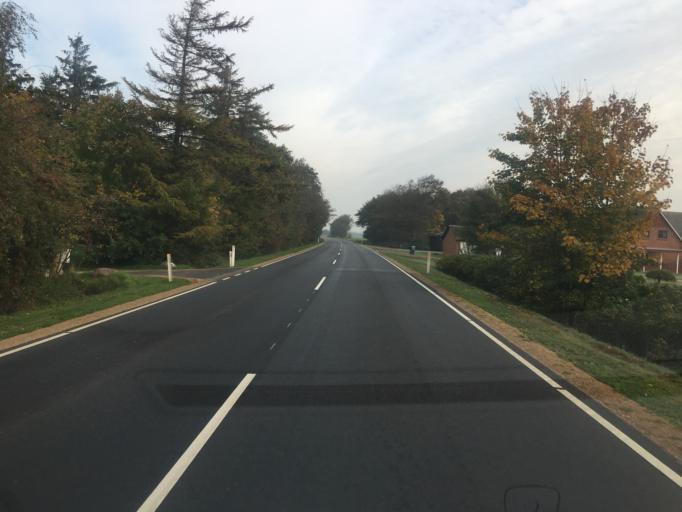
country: DK
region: South Denmark
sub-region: Tonder Kommune
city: Logumkloster
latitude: 55.0952
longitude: 9.0221
